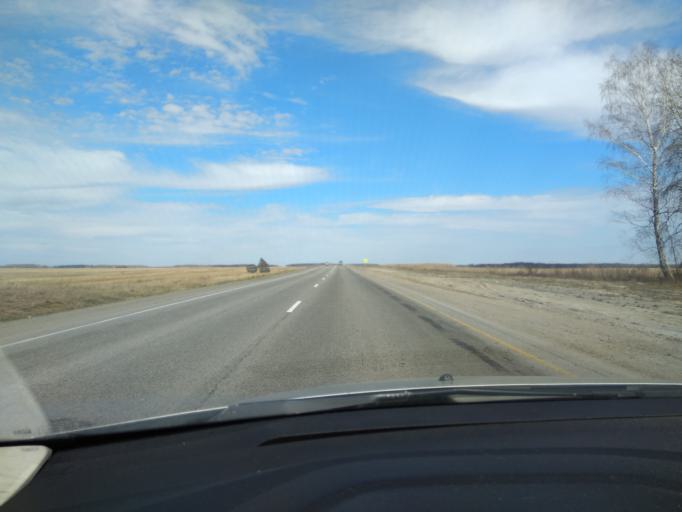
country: RU
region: Sverdlovsk
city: Pyshma
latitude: 56.9124
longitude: 63.1194
